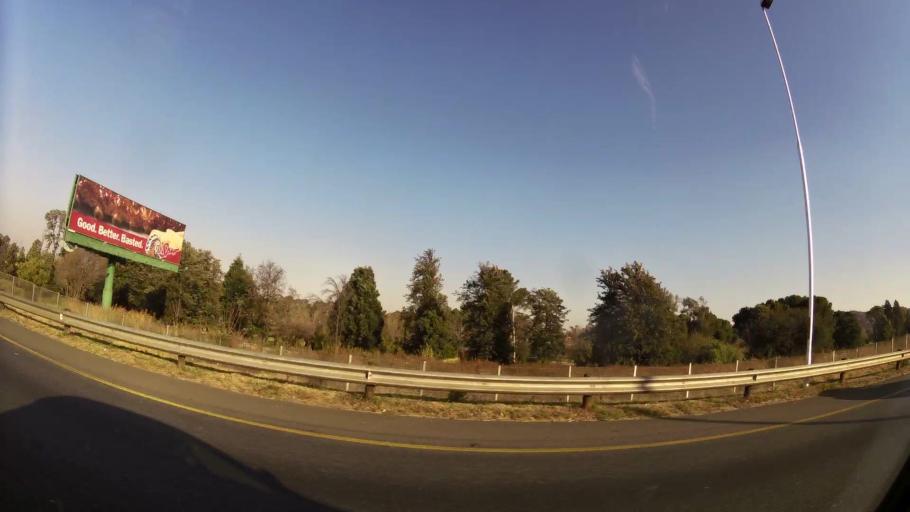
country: ZA
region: Gauteng
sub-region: Ekurhuleni Metropolitan Municipality
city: Germiston
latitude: -26.2602
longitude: 28.1099
